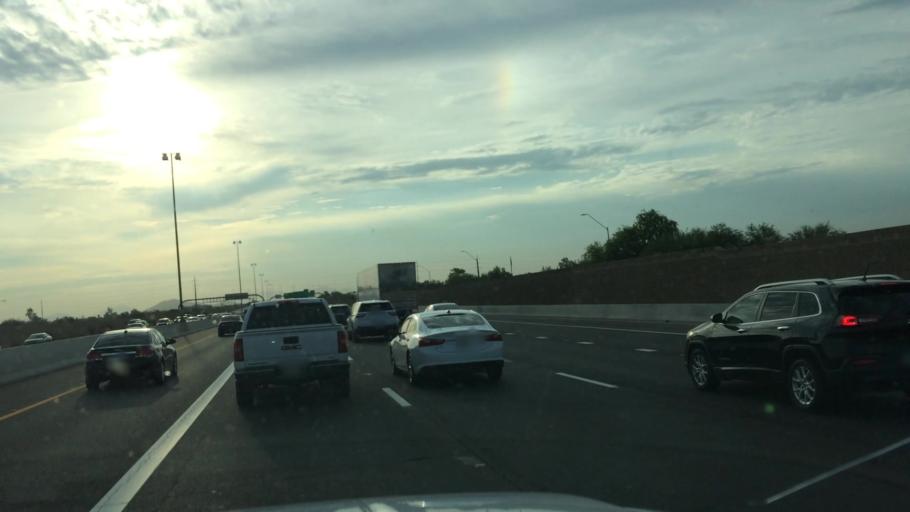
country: US
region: Arizona
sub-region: Maricopa County
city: Peoria
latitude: 33.6689
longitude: -112.1455
